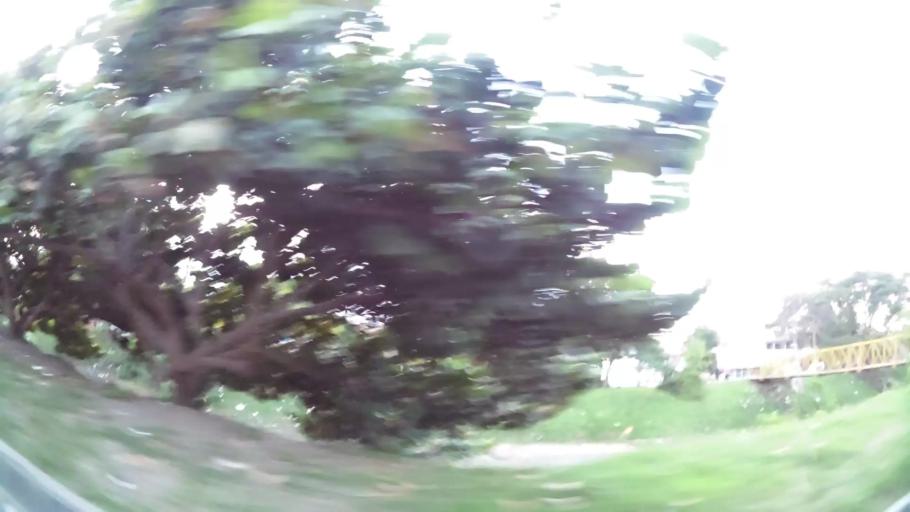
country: CO
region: Valle del Cauca
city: Cali
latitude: 3.4277
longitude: -76.4838
